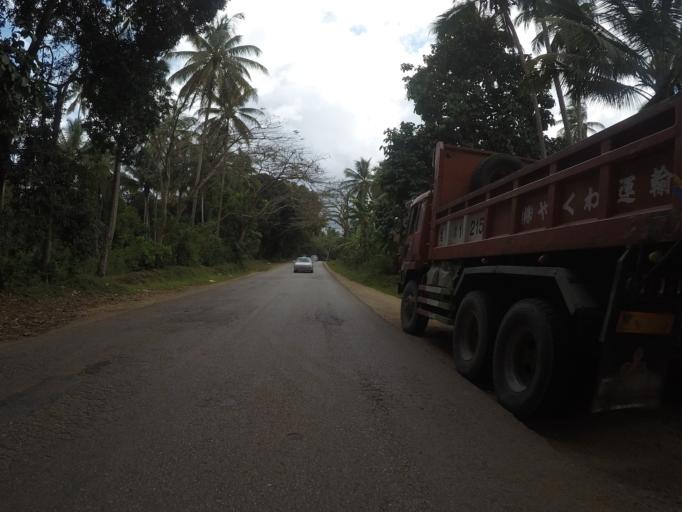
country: TZ
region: Zanzibar Central/South
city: Koani
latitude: -6.2088
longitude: 39.3244
